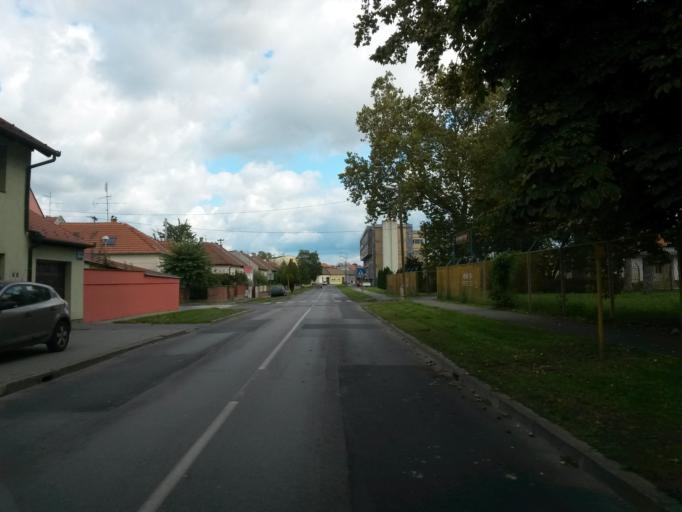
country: HR
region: Osjecko-Baranjska
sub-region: Grad Osijek
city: Osijek
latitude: 45.5570
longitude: 18.6617
